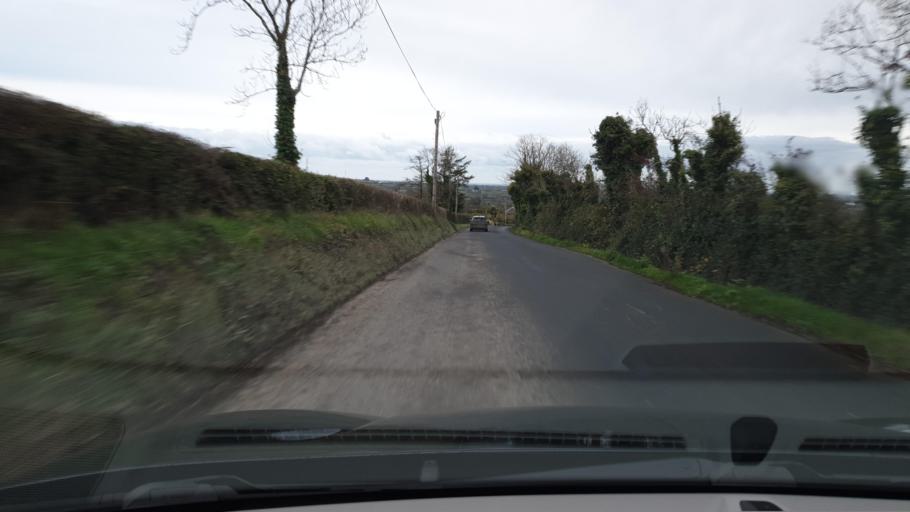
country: IE
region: Leinster
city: Balrothery
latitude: 53.5538
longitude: -6.2426
